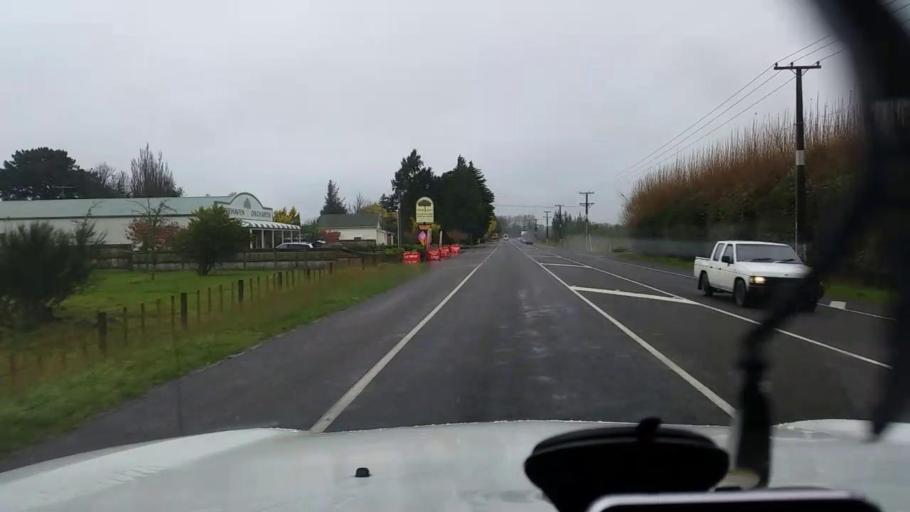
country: NZ
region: Wellington
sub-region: Masterton District
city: Masterton
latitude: -41.0718
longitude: 175.4700
